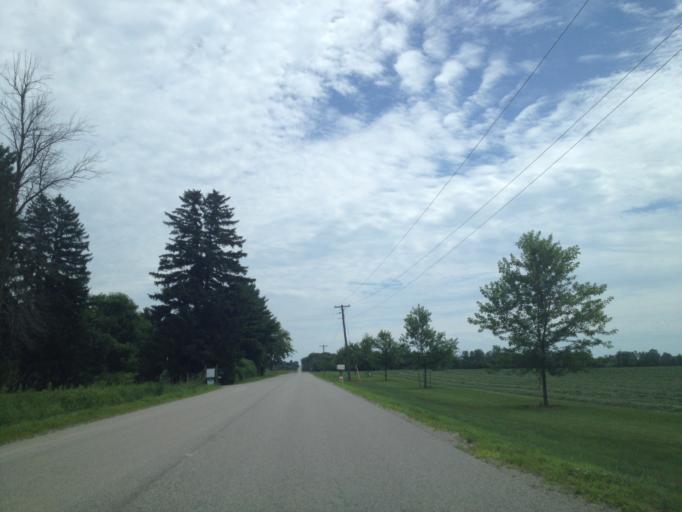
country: CA
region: Ontario
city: Ingersoll
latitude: 42.9725
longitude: -80.7995
